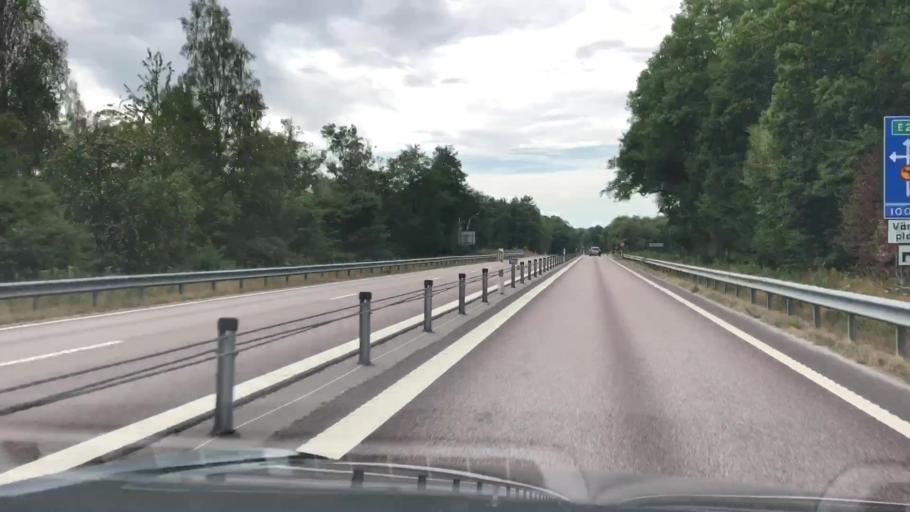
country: SE
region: Blekinge
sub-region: Karlskrona Kommun
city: Jaemjoe
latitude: 56.2308
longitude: 15.9157
